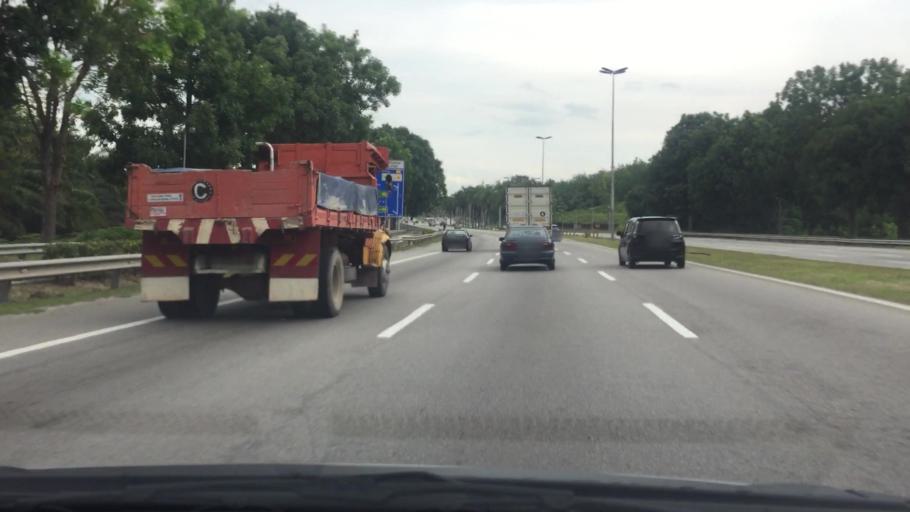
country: MY
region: Putrajaya
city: Putrajaya
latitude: 2.9052
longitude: 101.6585
